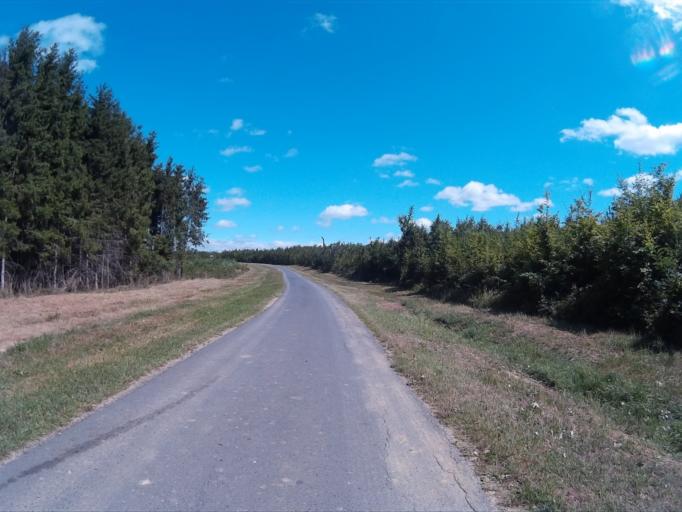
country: HU
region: Zala
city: Zalalovo
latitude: 46.7907
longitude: 16.6220
